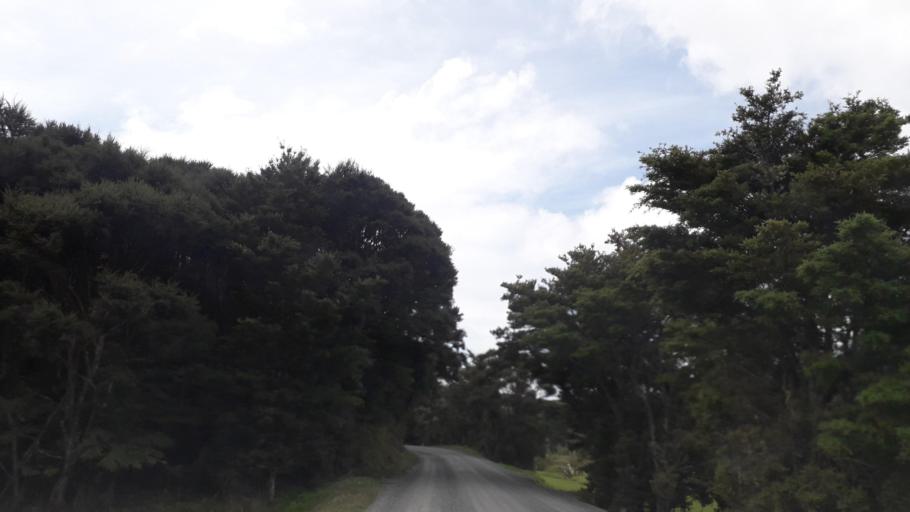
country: NZ
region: Northland
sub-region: Far North District
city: Taipa
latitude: -35.0488
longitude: 173.5597
